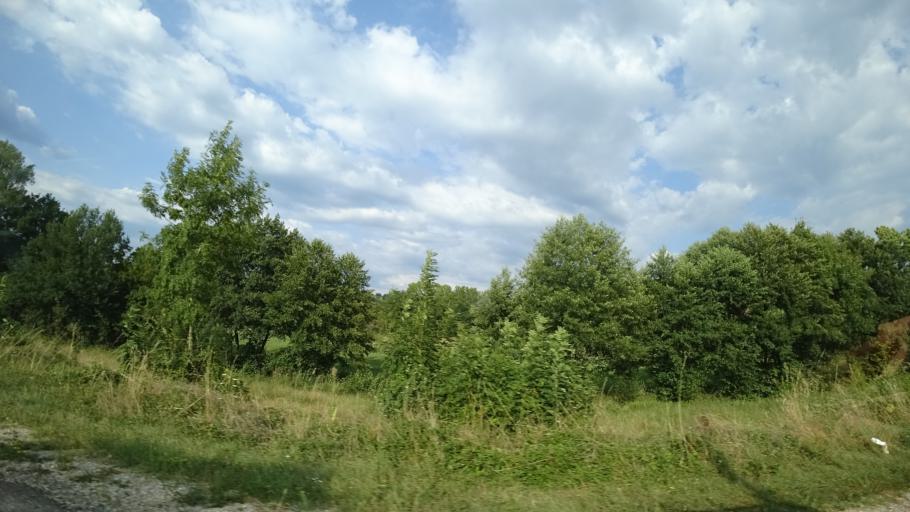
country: FR
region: Midi-Pyrenees
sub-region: Departement de l'Aveyron
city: Saint-Christophe-Vallon
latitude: 44.4921
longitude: 2.3883
